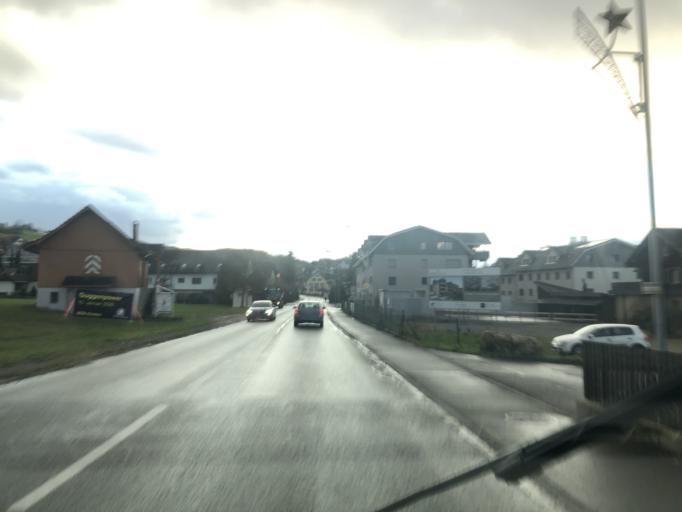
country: CH
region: Aargau
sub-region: Bezirk Baden
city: Kunten
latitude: 47.3922
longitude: 8.3276
